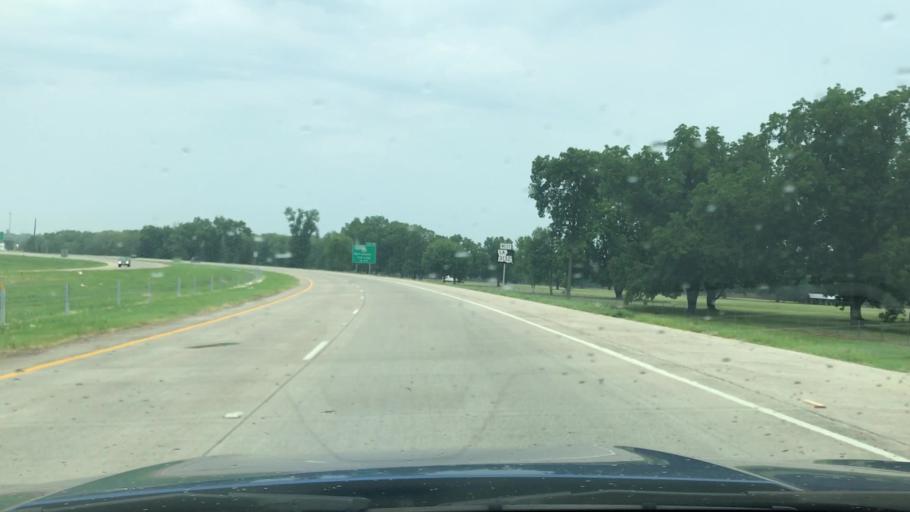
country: US
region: Louisiana
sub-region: Bossier Parish
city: Bossier City
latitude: 32.4070
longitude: -93.7151
